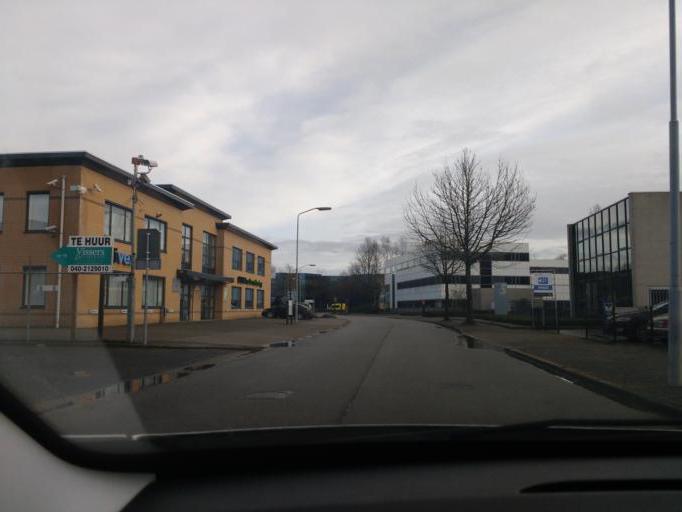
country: NL
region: North Brabant
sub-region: Gemeente Eindhoven
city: Meerhoven
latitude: 51.4550
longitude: 5.3941
